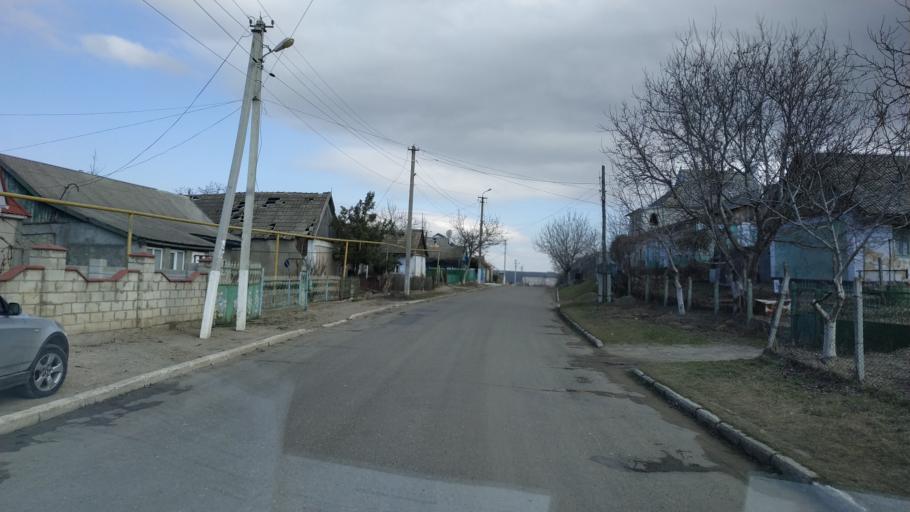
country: MD
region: Causeni
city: Causeni
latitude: 46.6443
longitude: 29.3880
